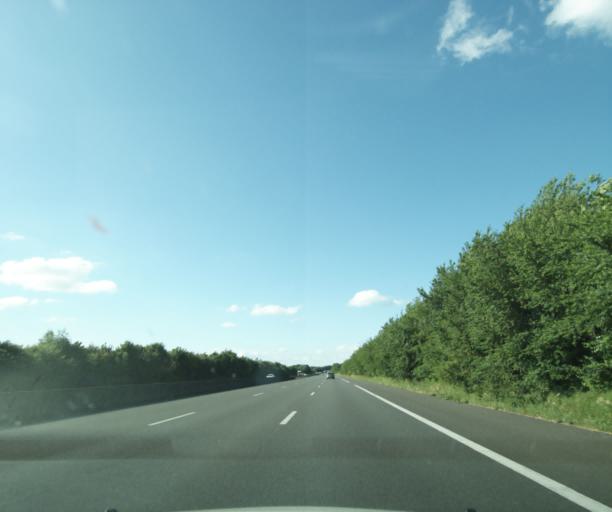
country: FR
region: Centre
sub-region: Departement d'Eure-et-Loir
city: Baigneaux
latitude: 48.1566
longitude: 1.8552
